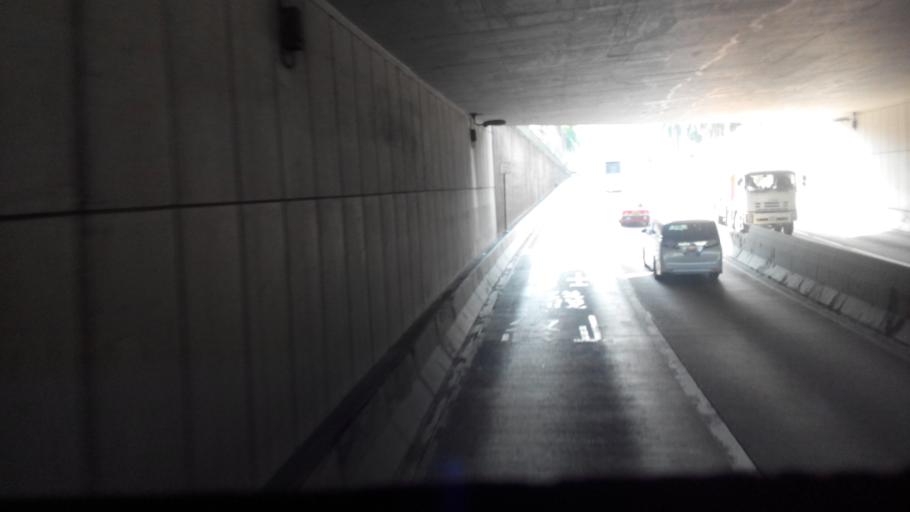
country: HK
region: Wanchai
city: Wan Chai
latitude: 22.2497
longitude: 114.1745
